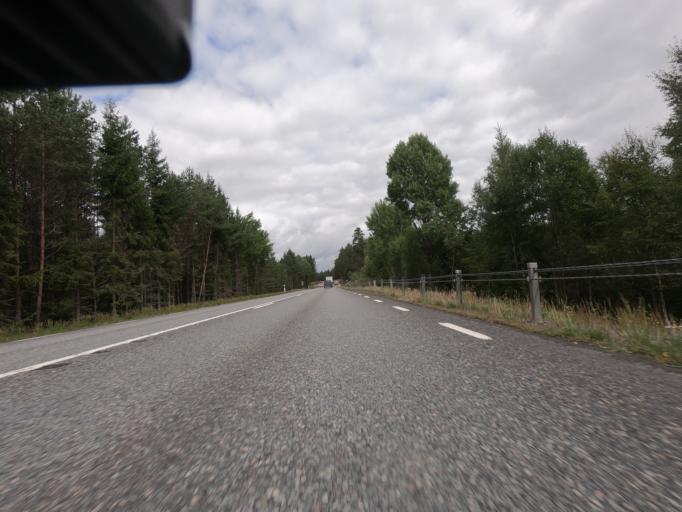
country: SE
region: Joenkoeping
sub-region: Vaggeryds Kommun
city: Vaggeryd
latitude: 57.4919
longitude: 14.2961
